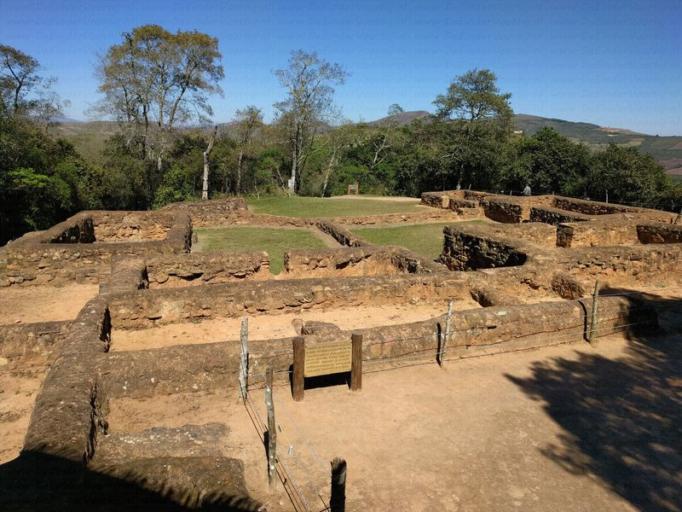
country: BO
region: Santa Cruz
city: Samaipata
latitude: -18.1795
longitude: -63.8217
